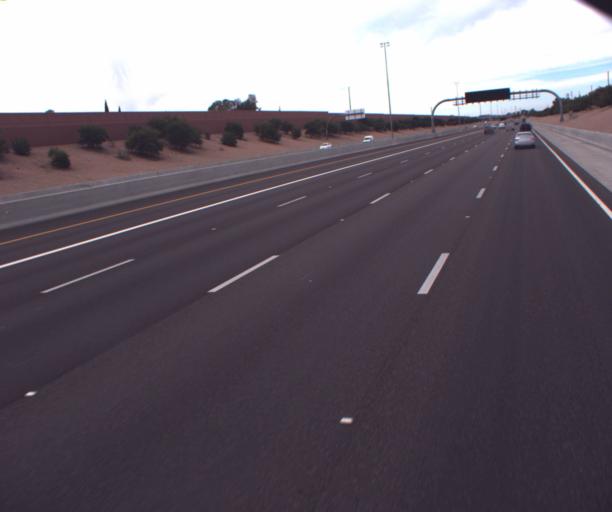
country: US
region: Arizona
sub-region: Maricopa County
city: Mesa
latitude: 33.4661
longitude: -111.8105
